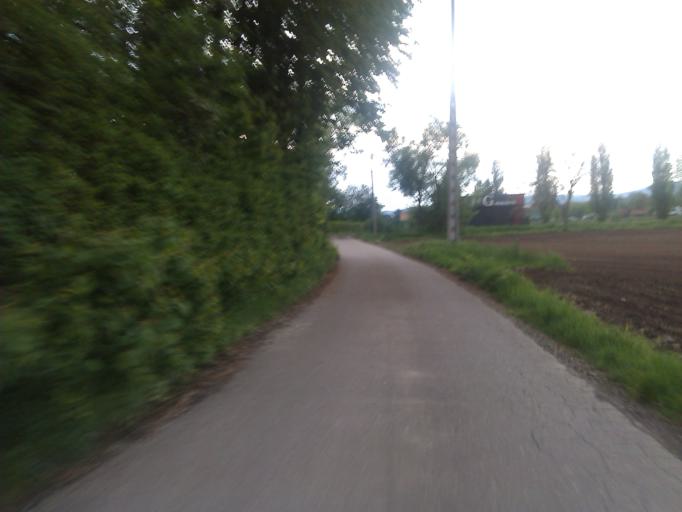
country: FR
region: Alsace
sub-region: Departement du Haut-Rhin
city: Ostheim
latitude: 48.1655
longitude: 7.3736
